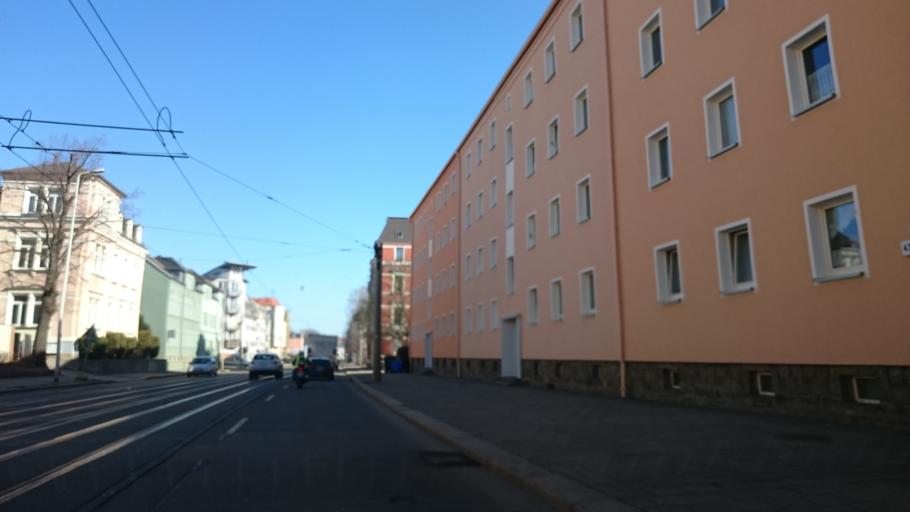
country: DE
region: Saxony
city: Weissenborn
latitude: 50.7201
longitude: 12.4683
